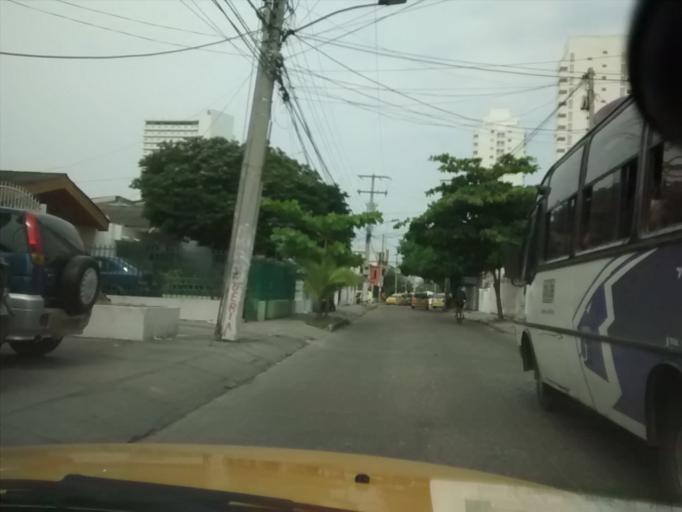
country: CO
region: Bolivar
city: Cartagena
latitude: 10.4104
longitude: -75.5348
